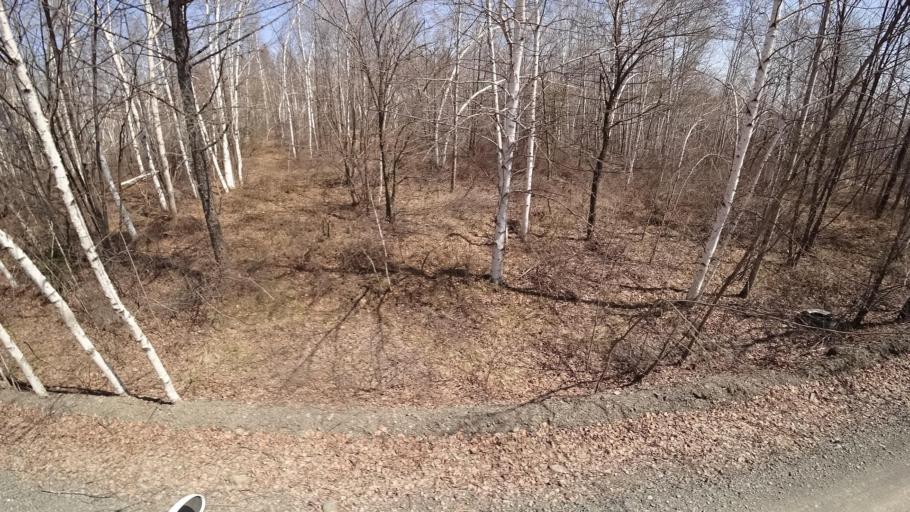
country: RU
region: Khabarovsk Krai
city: Khurba
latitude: 50.4119
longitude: 136.8433
